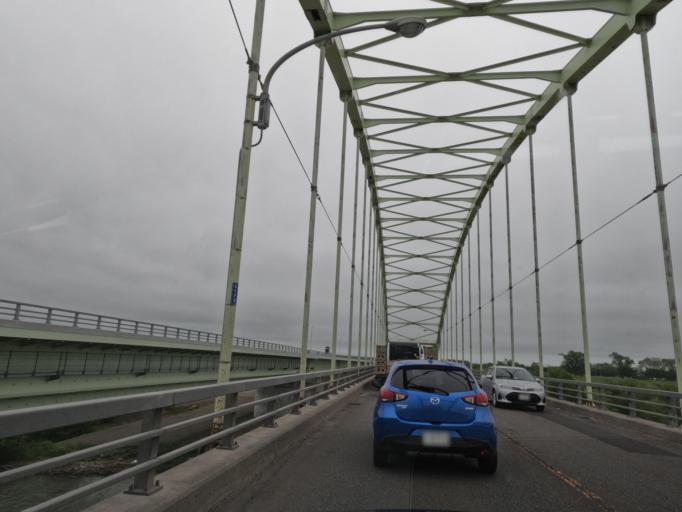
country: JP
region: Hokkaido
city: Ebetsu
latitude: 43.1361
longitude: 141.5119
